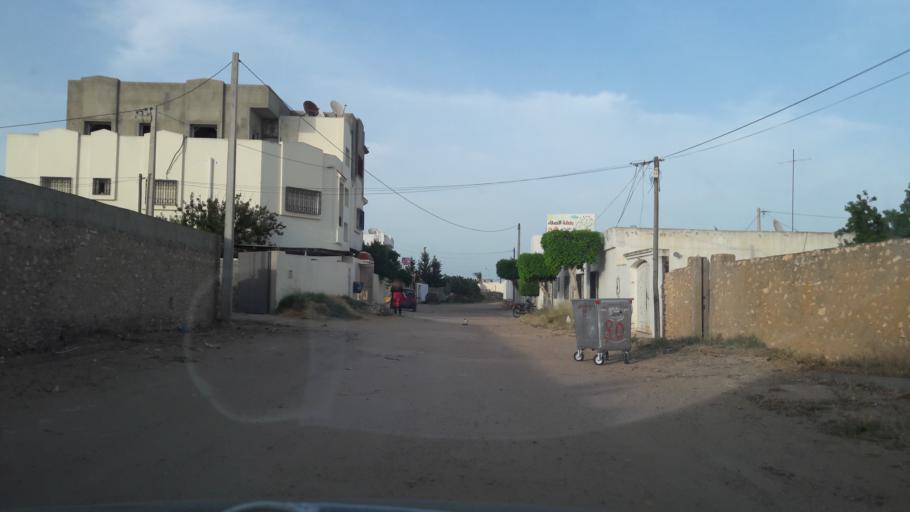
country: TN
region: Safaqis
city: Al Qarmadah
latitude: 34.8066
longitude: 10.7591
